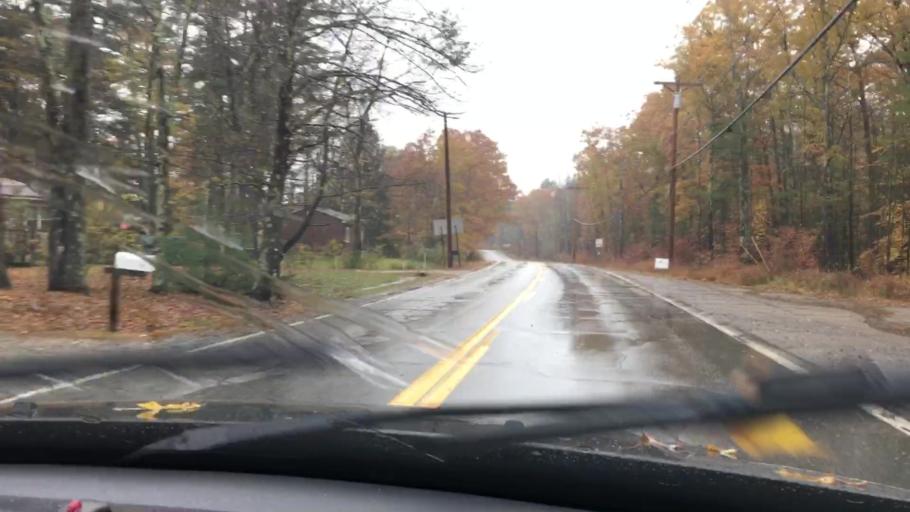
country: US
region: New Hampshire
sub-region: Belknap County
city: Meredith
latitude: 43.6993
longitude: -71.5173
